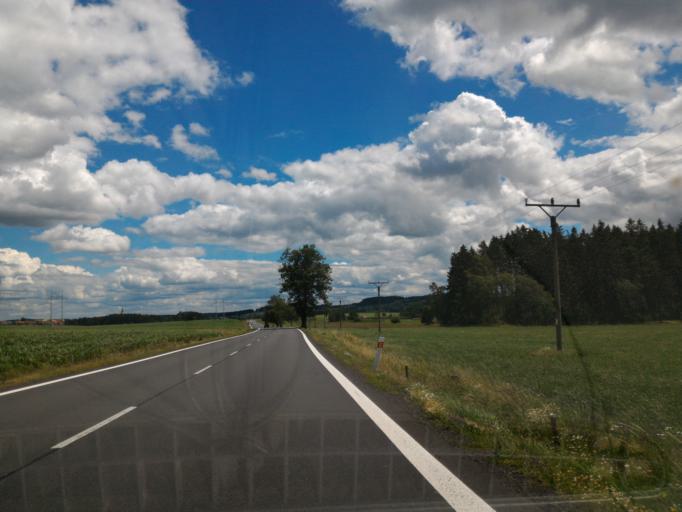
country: CZ
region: Vysocina
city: Bohdalov
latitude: 49.4786
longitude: 15.8451
